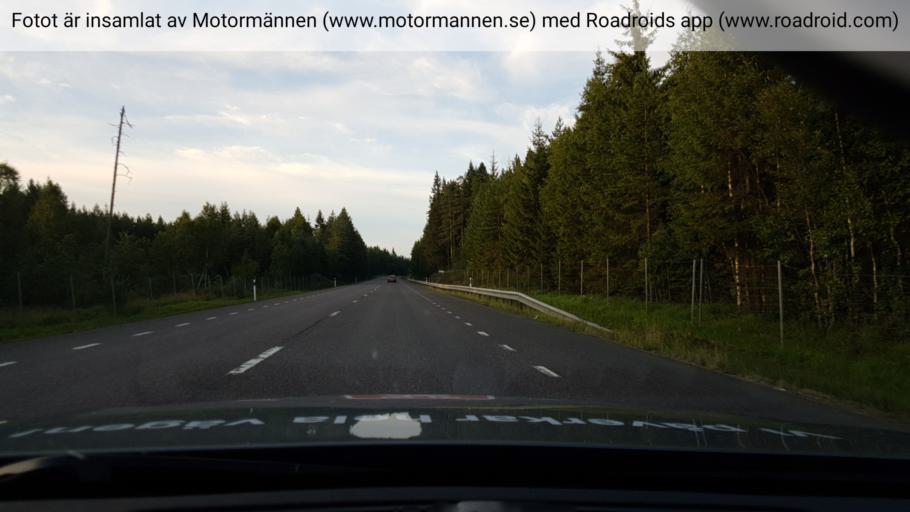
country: SE
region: Dalarna
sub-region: Ludvika Kommun
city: Grangesberg
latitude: 60.0813
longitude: 15.0383
